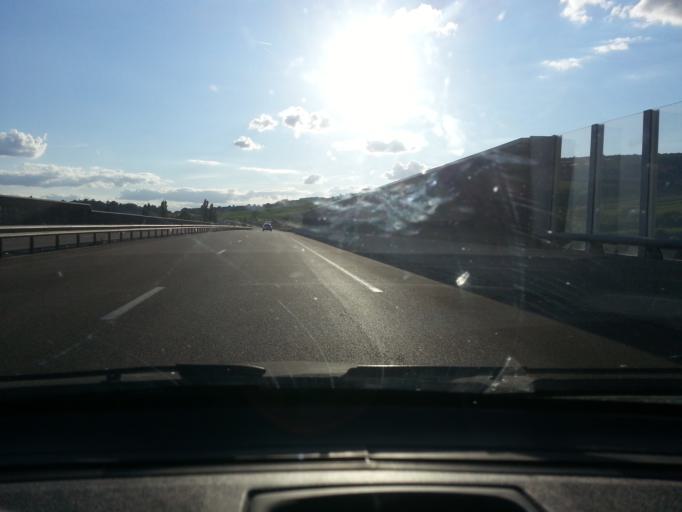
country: FR
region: Bourgogne
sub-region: Departement de Saone-et-Loire
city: Givry
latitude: 46.7568
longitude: 4.7083
